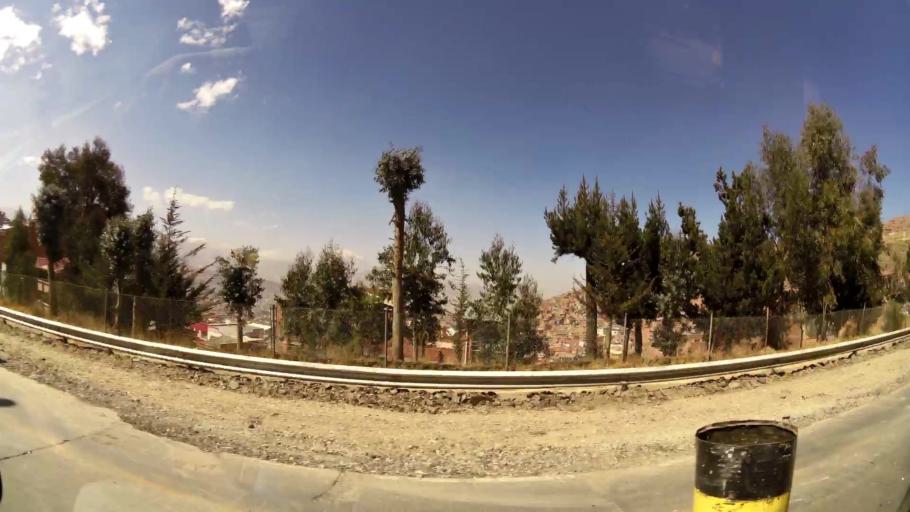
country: BO
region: La Paz
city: La Paz
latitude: -16.4879
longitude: -68.1688
